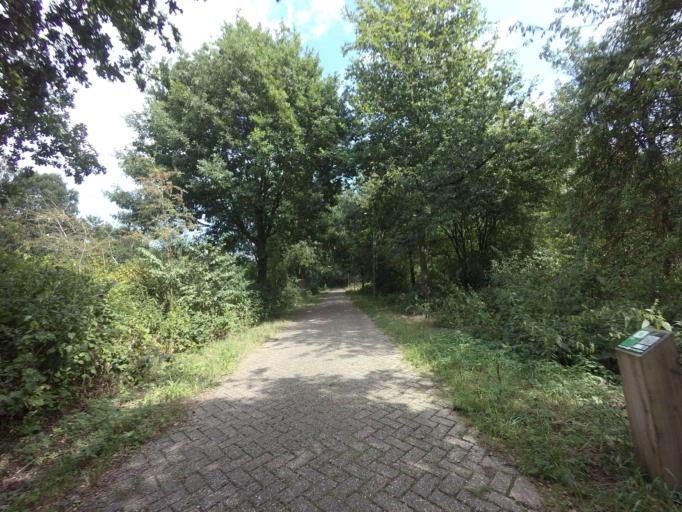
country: NL
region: Utrecht
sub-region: Gemeente Utrecht
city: Utrecht
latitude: 52.0953
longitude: 5.1488
